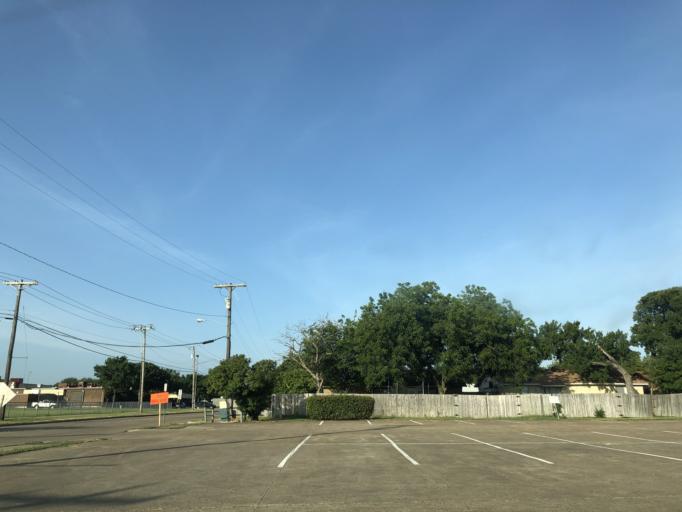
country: US
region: Texas
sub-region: Dallas County
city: Garland
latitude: 32.8685
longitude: -96.6113
